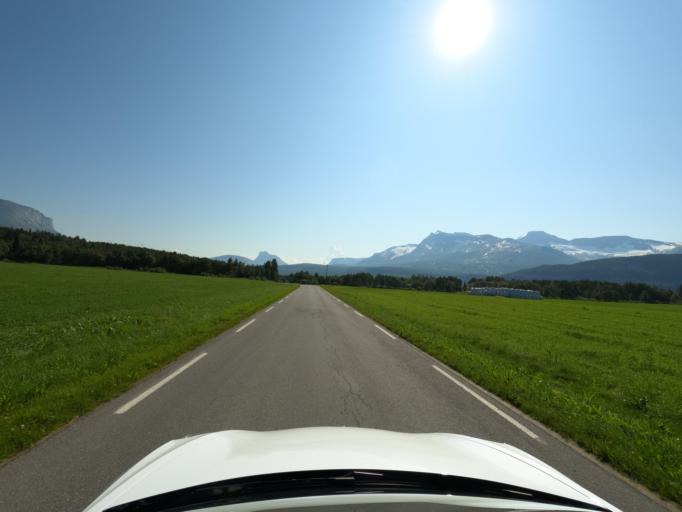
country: NO
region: Nordland
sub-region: Narvik
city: Narvik
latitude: 68.3223
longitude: 17.2892
